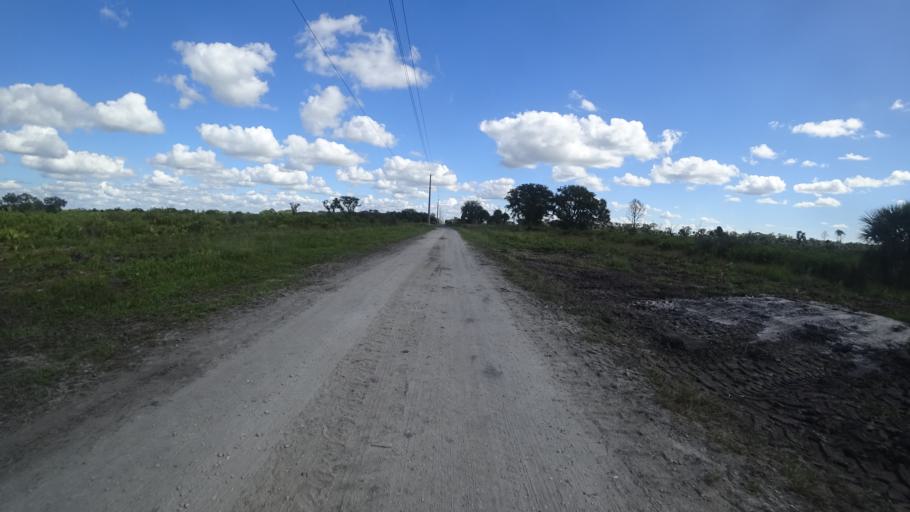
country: US
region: Florida
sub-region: Sarasota County
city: Lake Sarasota
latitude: 27.2480
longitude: -82.2850
